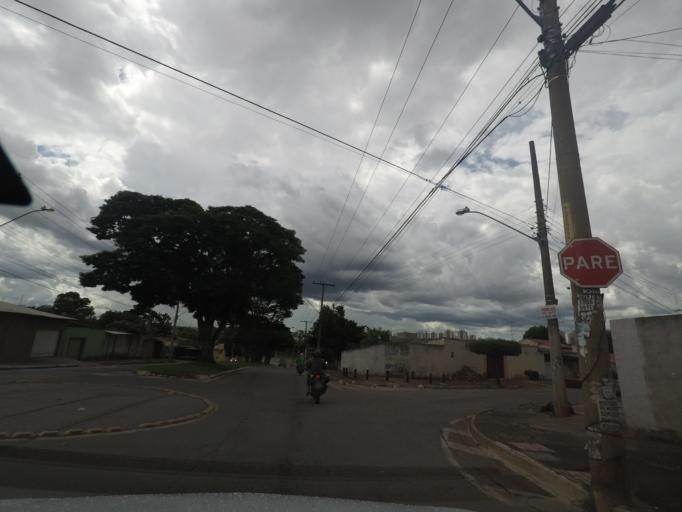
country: BR
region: Goias
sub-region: Goiania
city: Goiania
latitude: -16.7219
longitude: -49.3235
